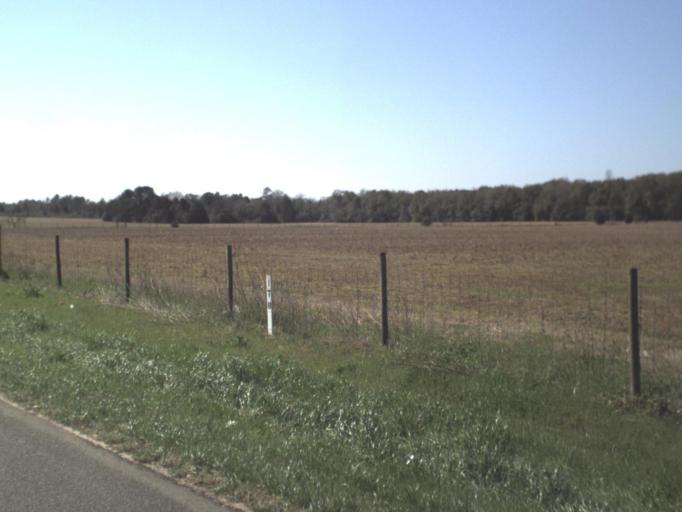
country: US
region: Florida
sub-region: Jackson County
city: Marianna
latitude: 30.6465
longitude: -85.1595
